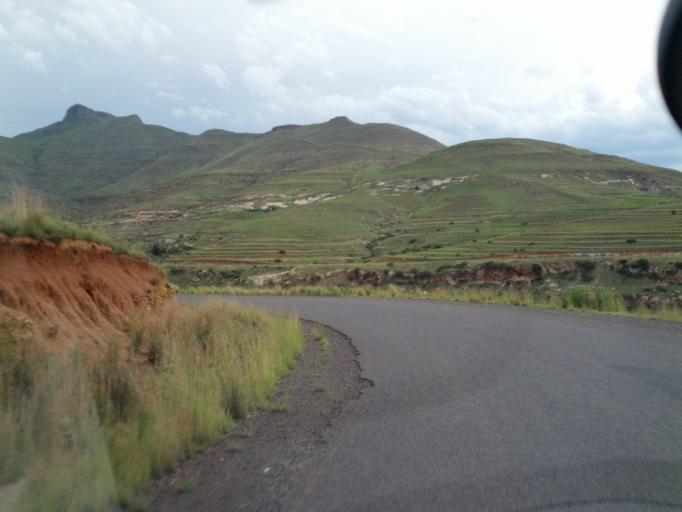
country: LS
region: Qacha's Nek
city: Qacha's Nek
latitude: -30.0729
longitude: 28.5824
